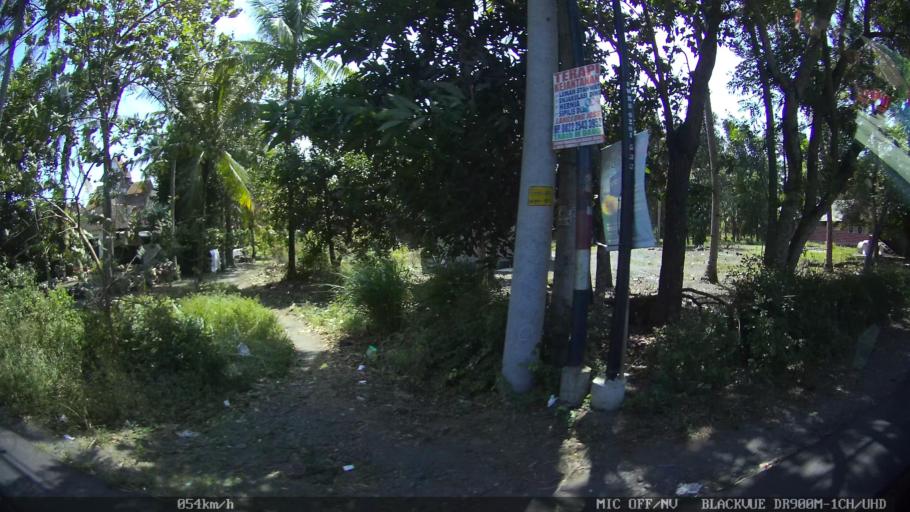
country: ID
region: Daerah Istimewa Yogyakarta
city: Srandakan
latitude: -7.9053
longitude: 110.0784
